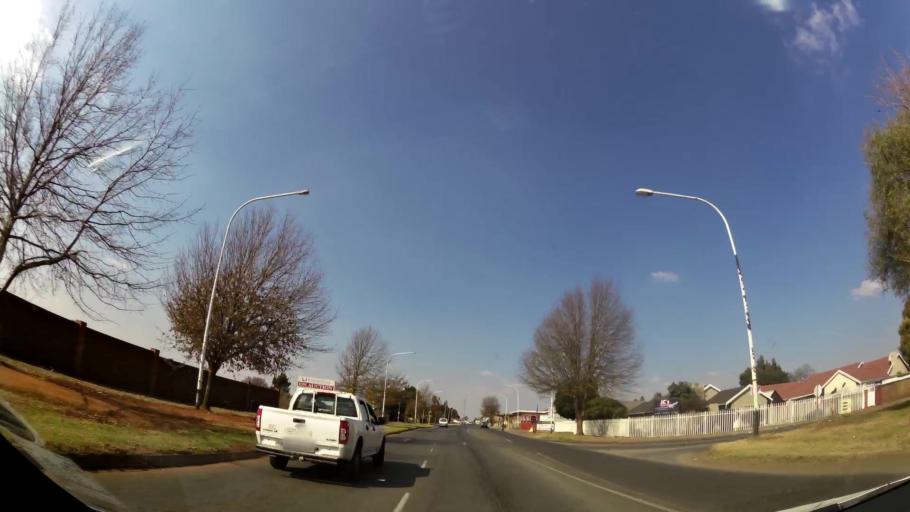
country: ZA
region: Gauteng
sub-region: Ekurhuleni Metropolitan Municipality
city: Boksburg
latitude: -26.1880
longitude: 28.2226
